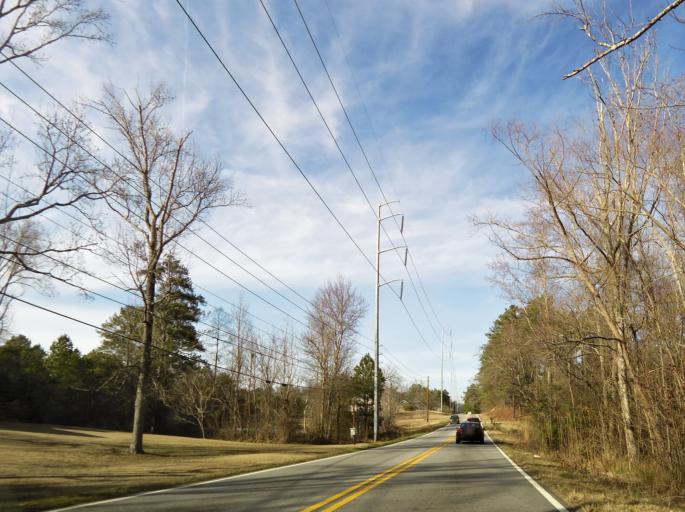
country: US
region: Georgia
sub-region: Bibb County
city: West Point
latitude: 32.8366
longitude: -83.7451
